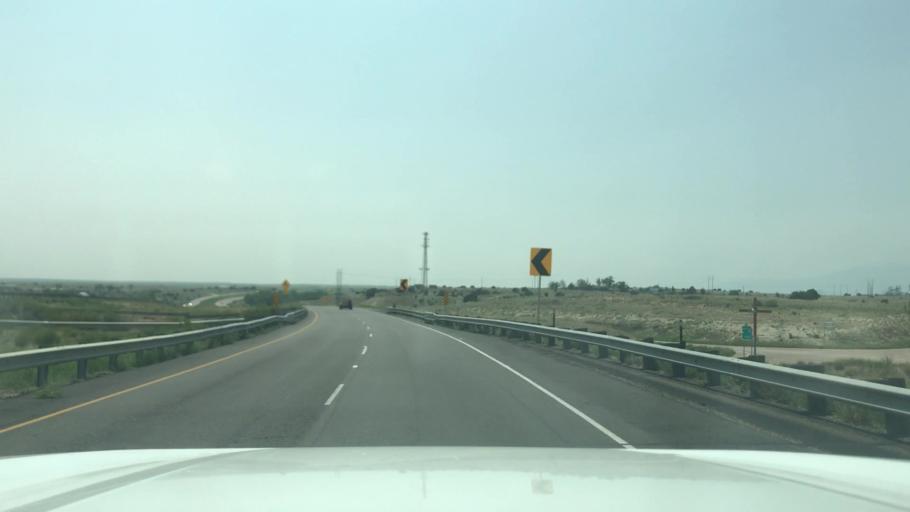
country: US
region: Colorado
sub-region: Pueblo County
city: Pueblo
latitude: 38.1290
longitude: -104.6700
